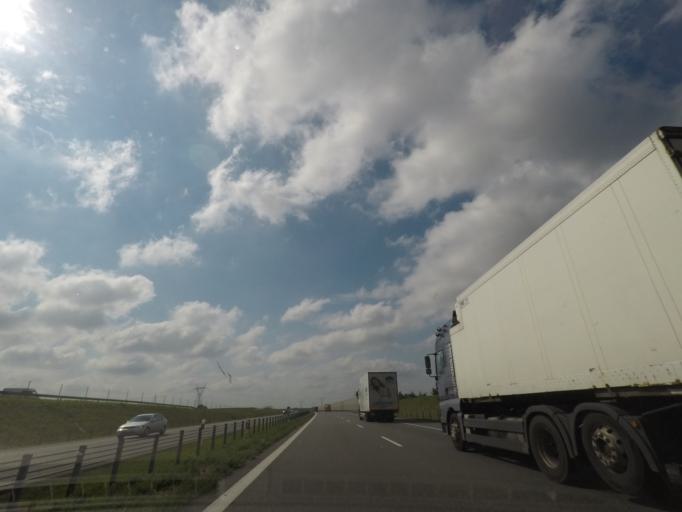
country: PL
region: Kujawsko-Pomorskie
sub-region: Powiat chelminski
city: Lisewo
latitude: 53.2397
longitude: 18.7253
